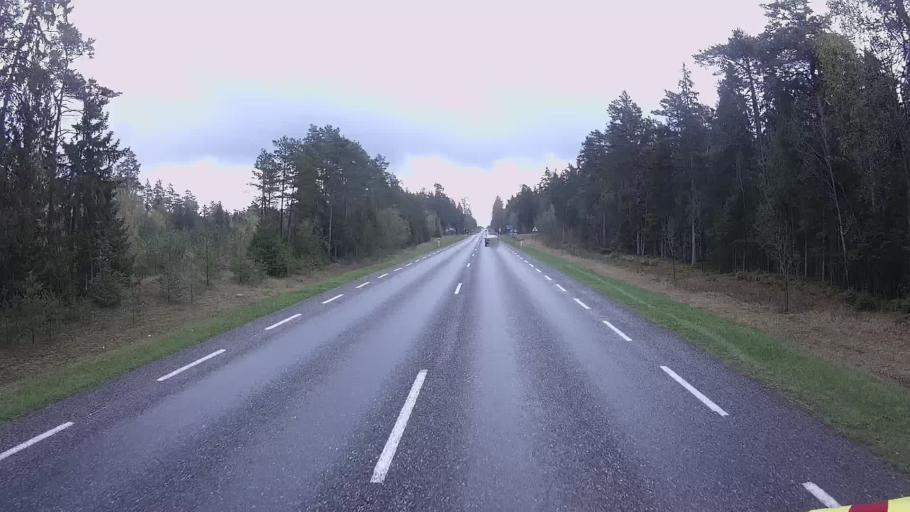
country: EE
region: Hiiumaa
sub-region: Kaerdla linn
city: Kardla
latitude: 58.9644
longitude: 22.8382
